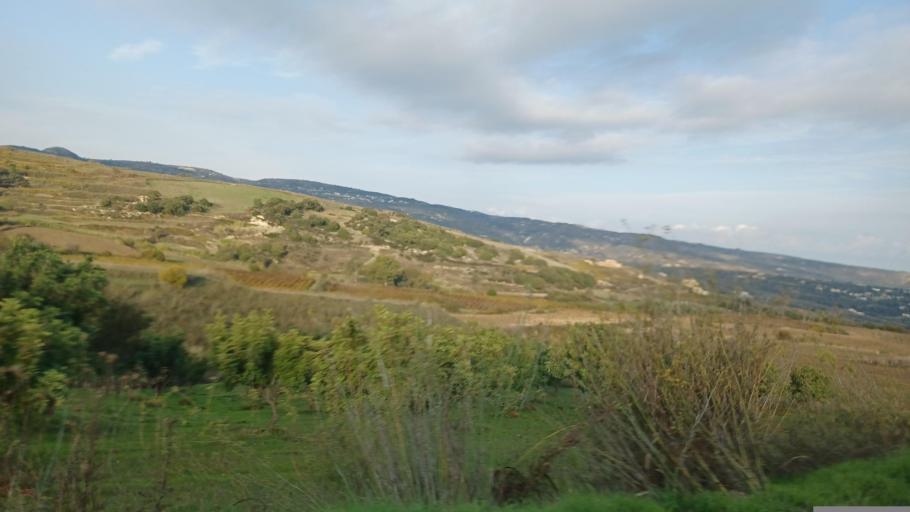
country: CY
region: Pafos
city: Tala
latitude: 34.9004
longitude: 32.4869
